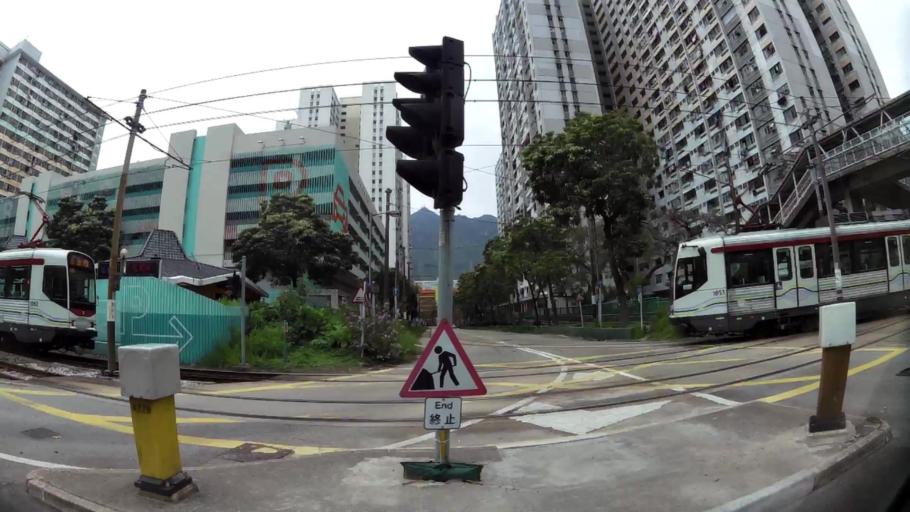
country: HK
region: Tuen Mun
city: Tuen Mun
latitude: 22.3885
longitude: 113.9752
